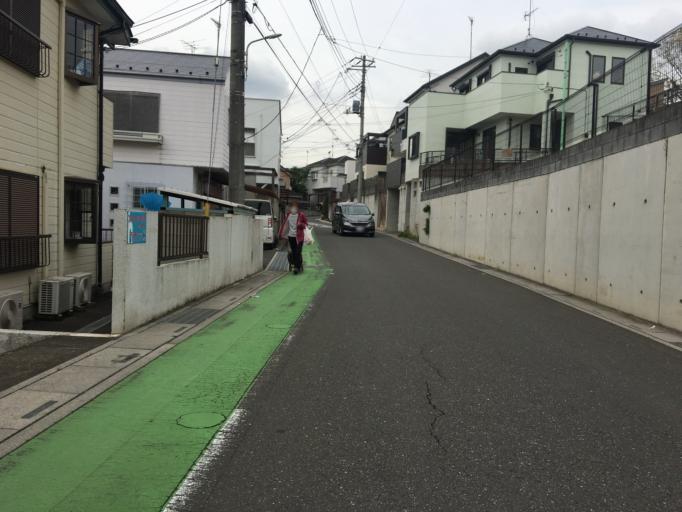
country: JP
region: Saitama
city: Oi
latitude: 35.8511
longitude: 139.5466
